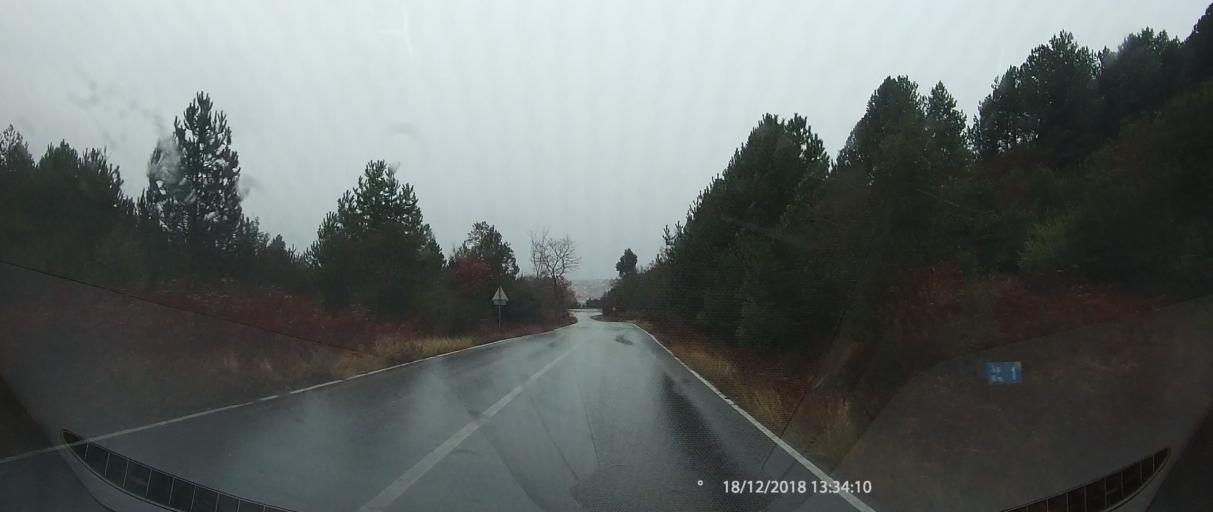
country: GR
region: Central Macedonia
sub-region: Nomos Pierias
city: Litochoro
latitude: 40.1137
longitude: 22.4844
